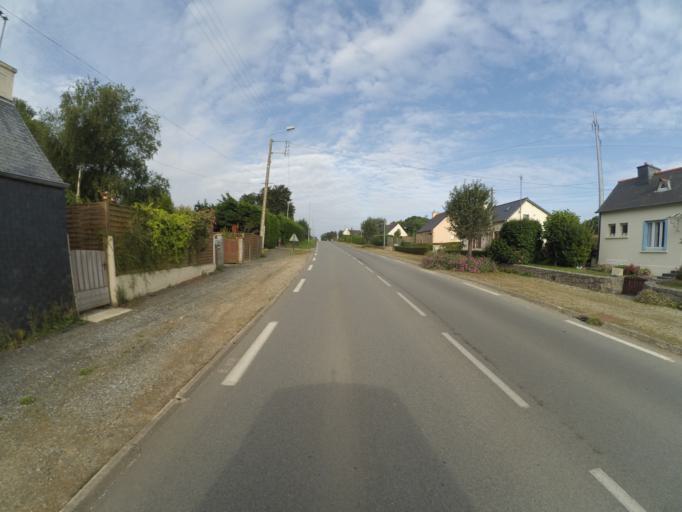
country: FR
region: Brittany
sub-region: Departement des Cotes-d'Armor
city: Graces
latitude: 48.5667
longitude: -3.1838
